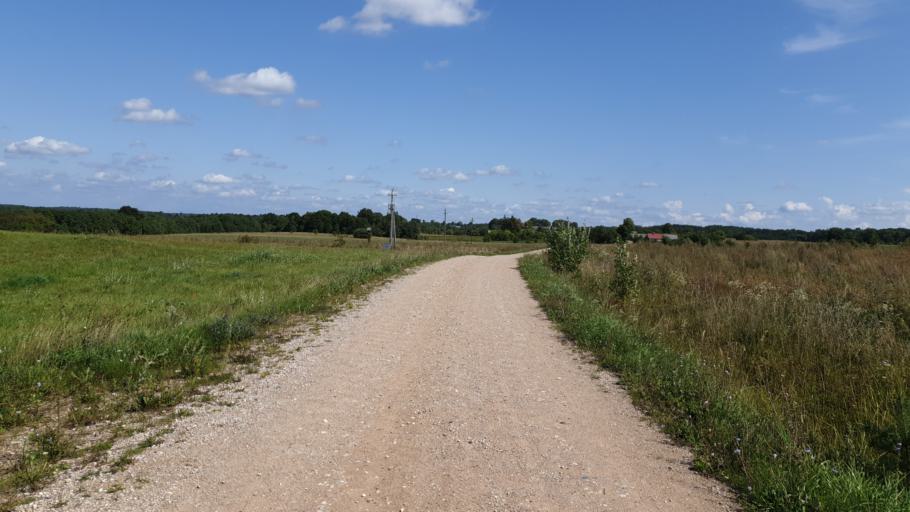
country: LT
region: Vilnius County
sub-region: Vilniaus Rajonas
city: Vievis
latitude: 54.8211
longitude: 24.9444
